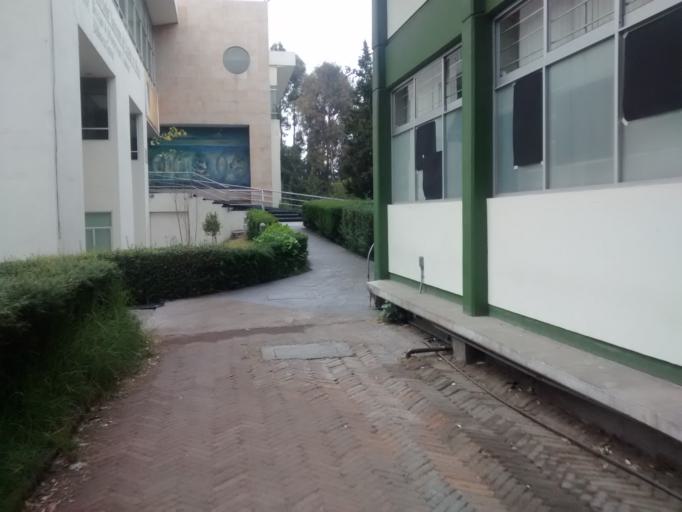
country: MX
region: Mexico
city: San Buenaventura
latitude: 19.2868
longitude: -99.6792
